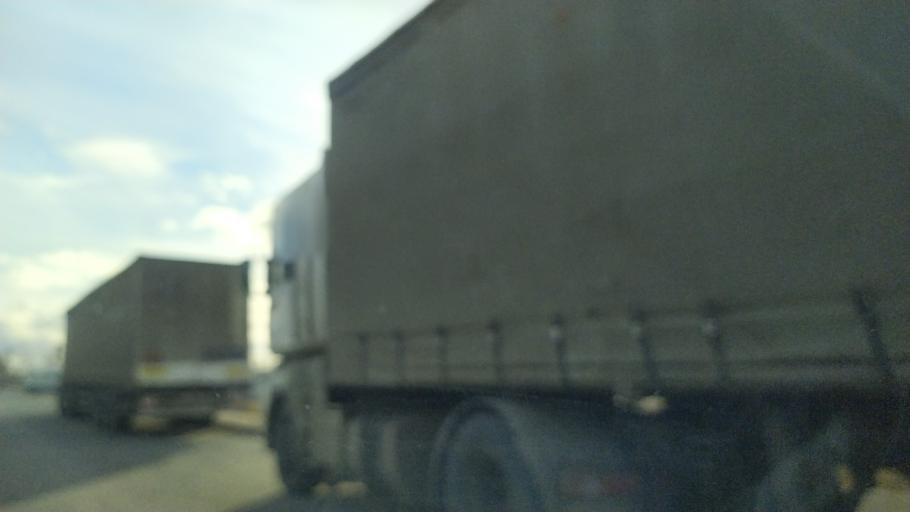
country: RU
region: St.-Petersburg
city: Petro-Slavyanka
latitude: 59.7742
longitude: 30.4577
